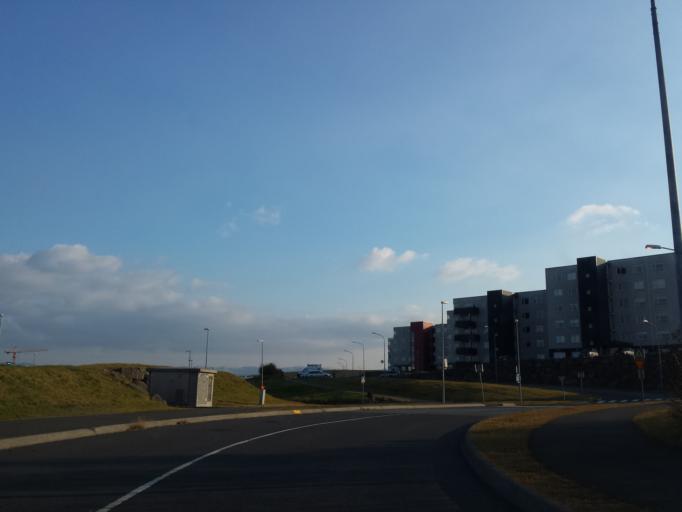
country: IS
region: Capital Region
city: Reykjavik
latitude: 64.0868
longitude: -21.8343
